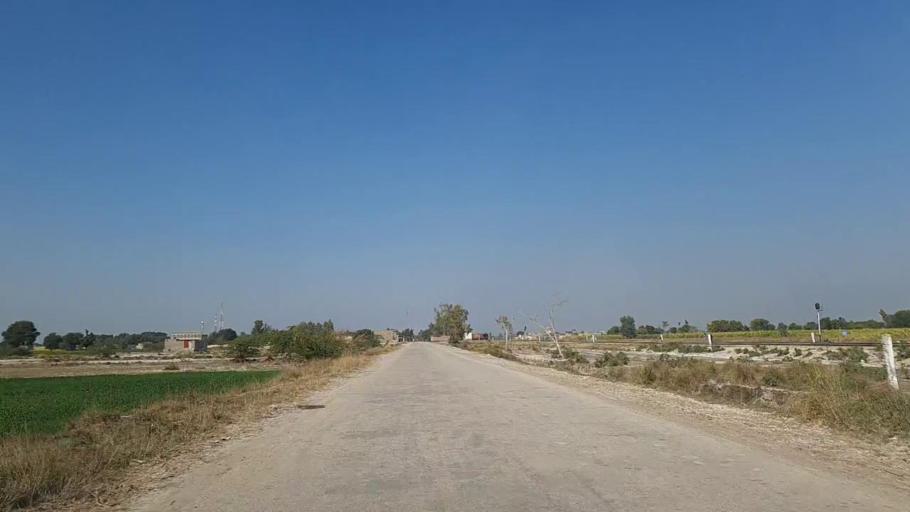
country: PK
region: Sindh
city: Nawabshah
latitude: 26.3457
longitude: 68.3685
